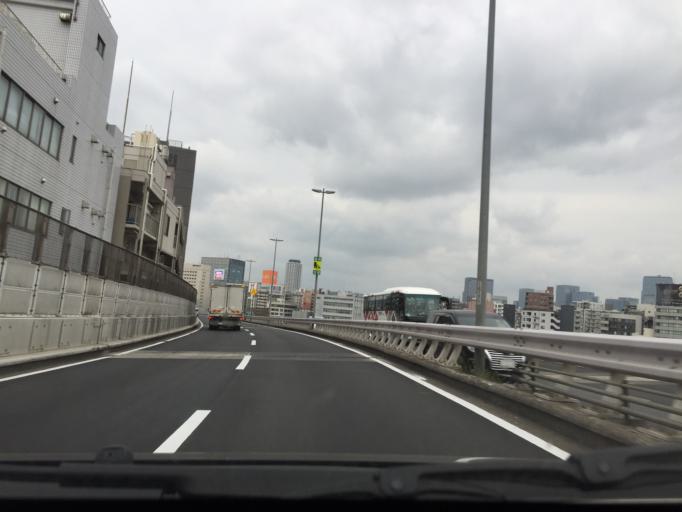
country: JP
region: Tokyo
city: Tokyo
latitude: 35.6957
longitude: 139.7903
